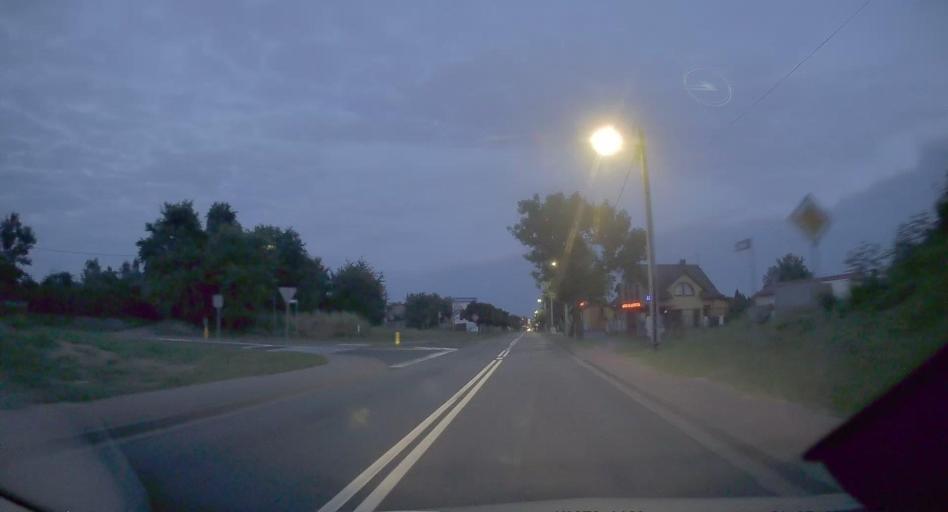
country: PL
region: Silesian Voivodeship
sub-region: Powiat klobucki
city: Klobuck
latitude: 50.9051
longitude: 18.9237
